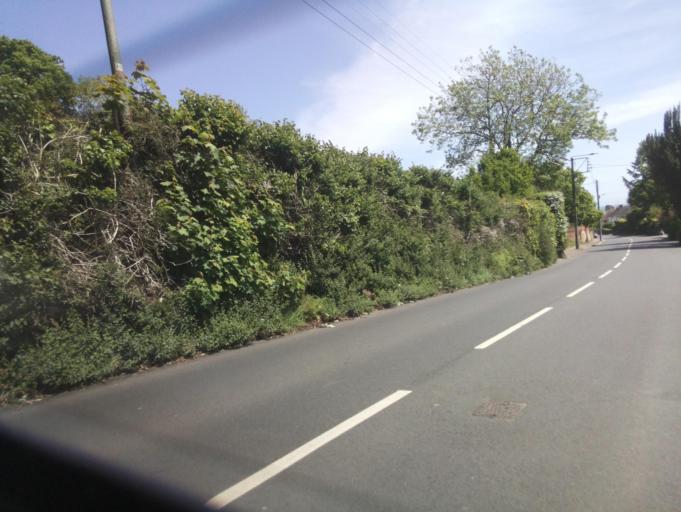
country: GB
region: England
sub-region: Devon
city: Budleigh Salterton
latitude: 50.6298
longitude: -3.3334
